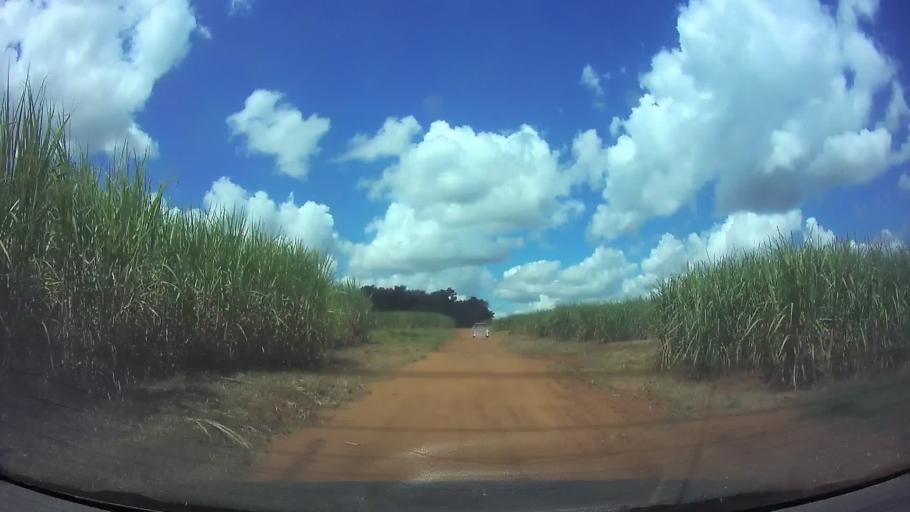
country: PY
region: Paraguari
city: La Colmena
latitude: -25.9510
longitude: -56.7805
